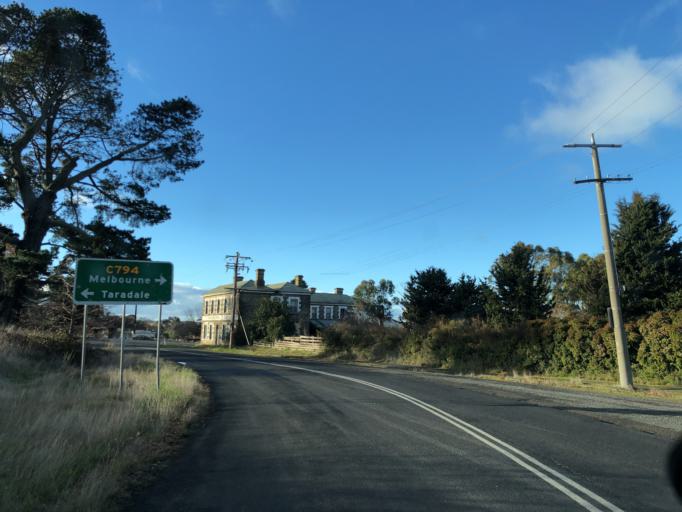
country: AU
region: Victoria
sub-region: Mount Alexander
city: Castlemaine
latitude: -37.1886
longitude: 144.3752
